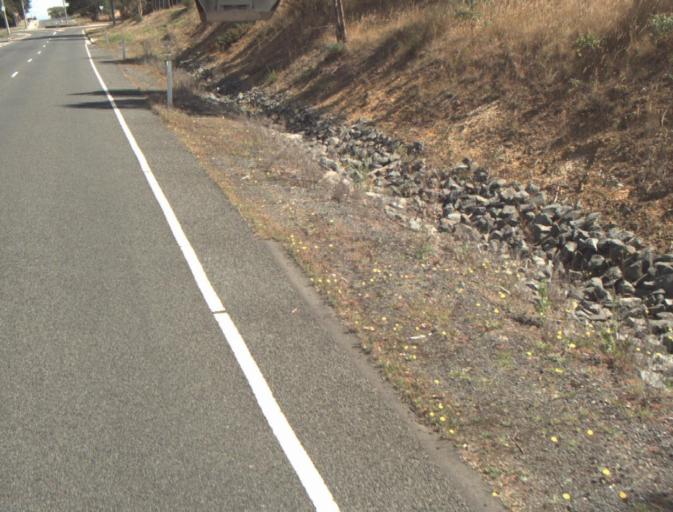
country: AU
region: Tasmania
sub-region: Launceston
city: Newstead
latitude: -41.4238
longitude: 147.1829
